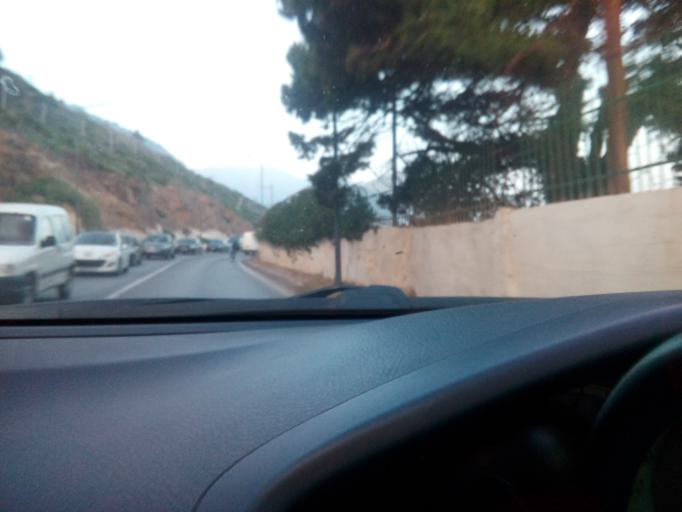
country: DZ
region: Oran
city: Oran
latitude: 35.7135
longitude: -0.6682
